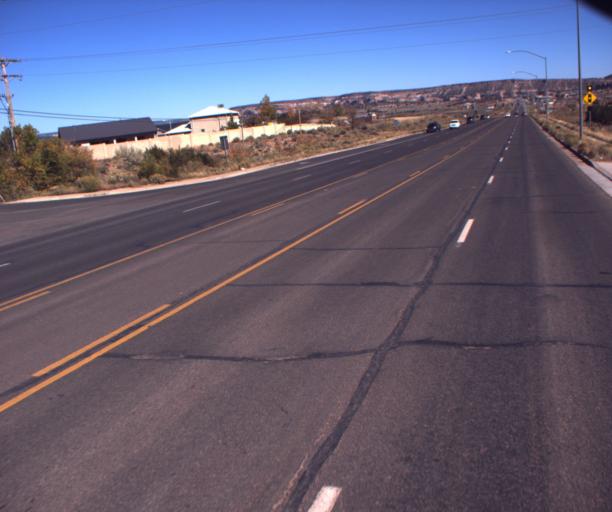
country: US
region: Arizona
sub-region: Apache County
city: Saint Michaels
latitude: 35.6565
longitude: -109.0928
